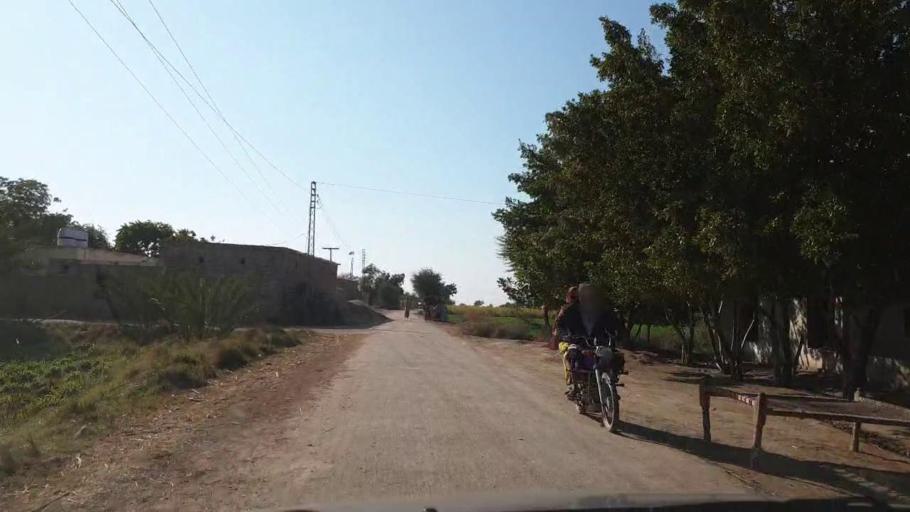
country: PK
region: Sindh
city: Khadro
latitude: 26.1556
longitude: 68.7745
